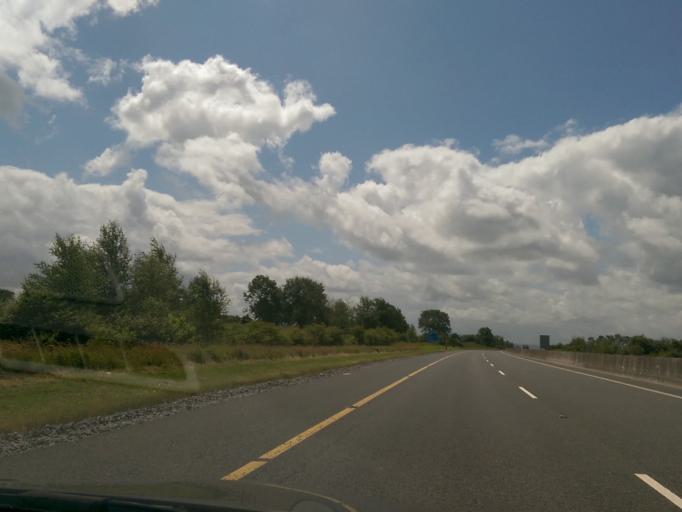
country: IE
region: Munster
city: Cahir
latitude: 52.3474
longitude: -8.0084
